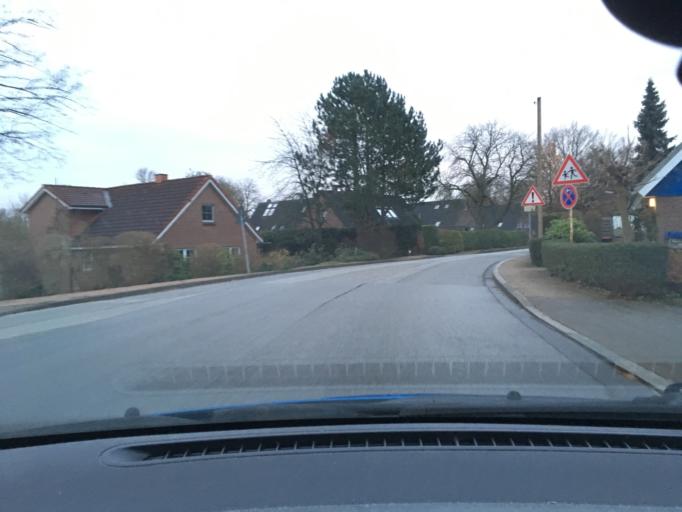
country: DE
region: Lower Saxony
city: Winsen
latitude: 53.4120
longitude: 10.2107
